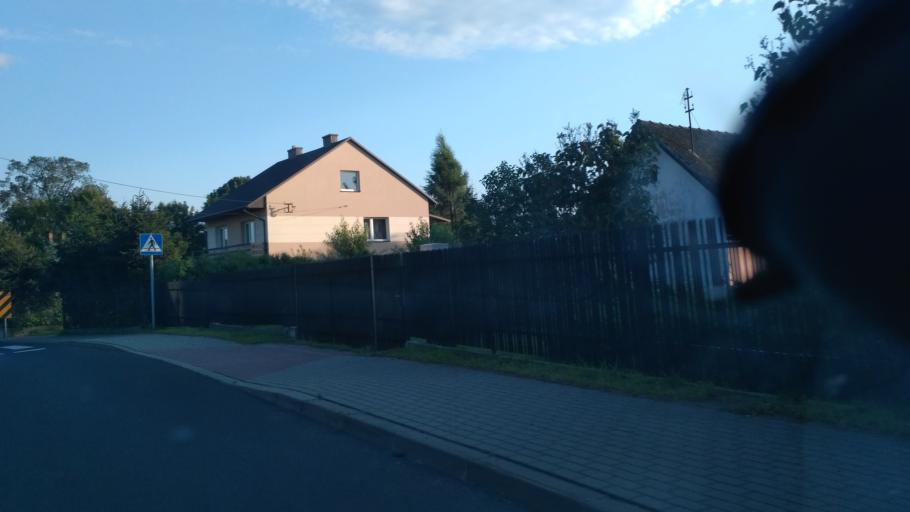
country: PL
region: Subcarpathian Voivodeship
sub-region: Powiat lezajski
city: Stare Miasto
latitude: 50.2838
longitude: 22.4299
